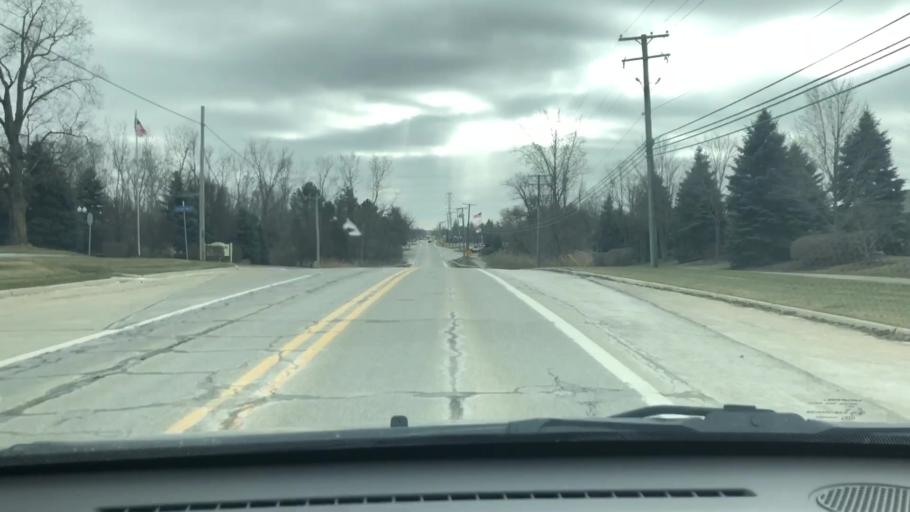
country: US
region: Michigan
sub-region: Macomb County
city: Shelby
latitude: 42.7382
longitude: -83.0365
